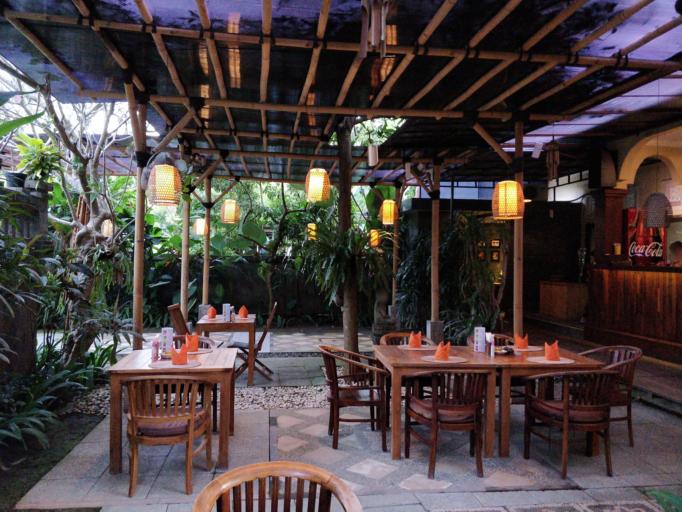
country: ID
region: Bali
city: Banjar Pegeringsingan
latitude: -8.5019
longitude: 115.5530
